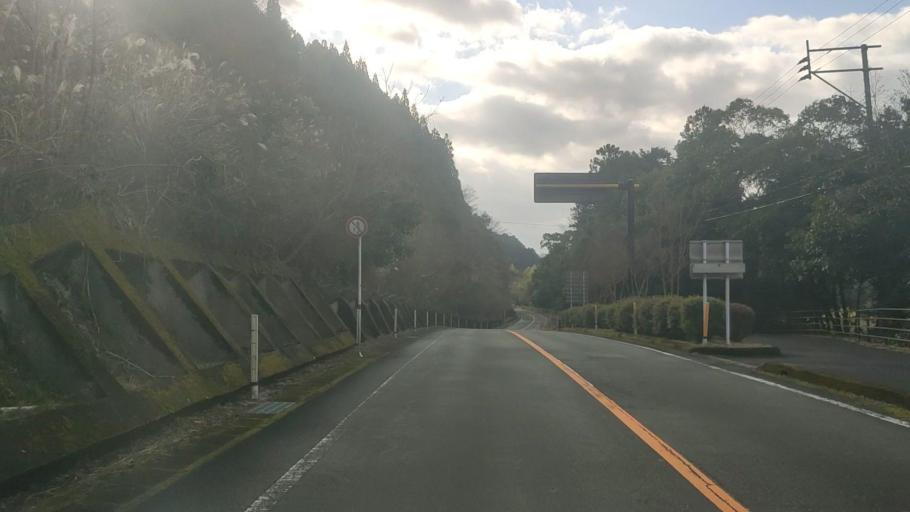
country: JP
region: Kumamoto
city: Hitoyoshi
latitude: 32.3115
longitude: 130.8478
